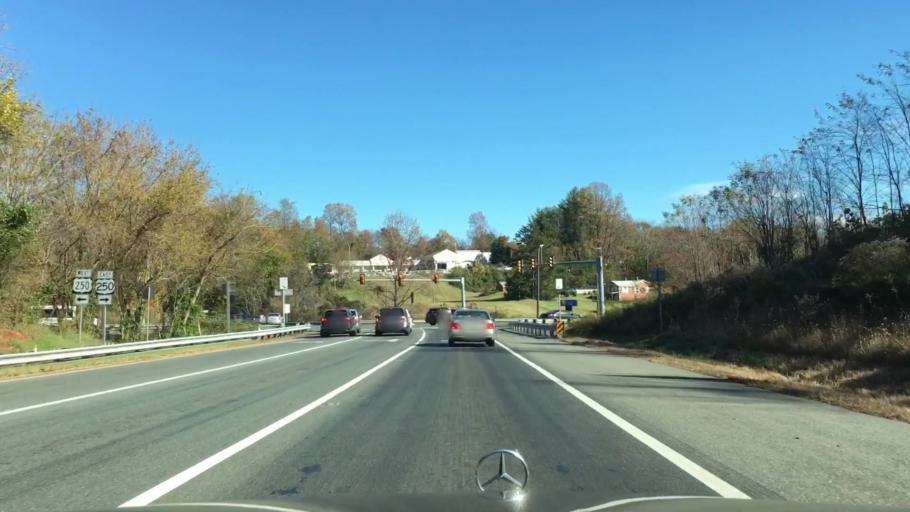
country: US
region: Virginia
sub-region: City of Charlottesville
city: Charlottesville
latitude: 38.0195
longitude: -78.4307
